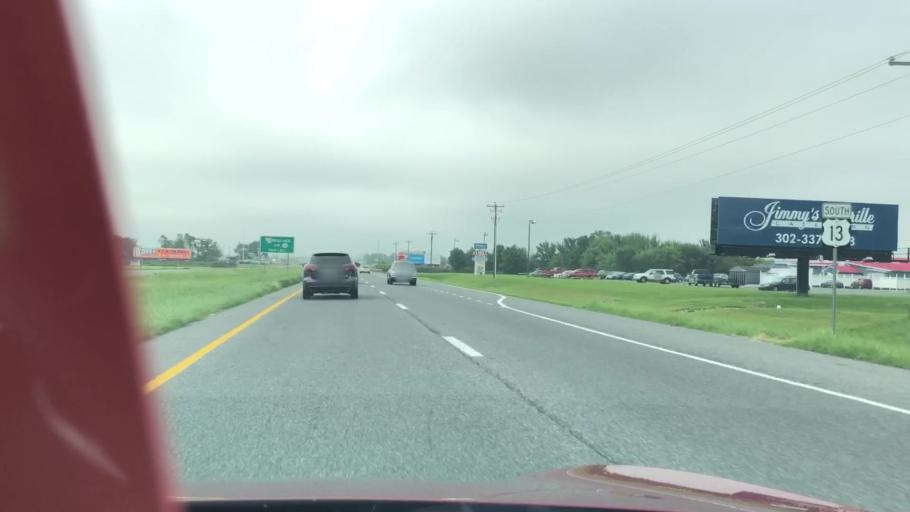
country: US
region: Delaware
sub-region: Sussex County
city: Bridgeville
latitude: 38.7297
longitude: -75.5913
